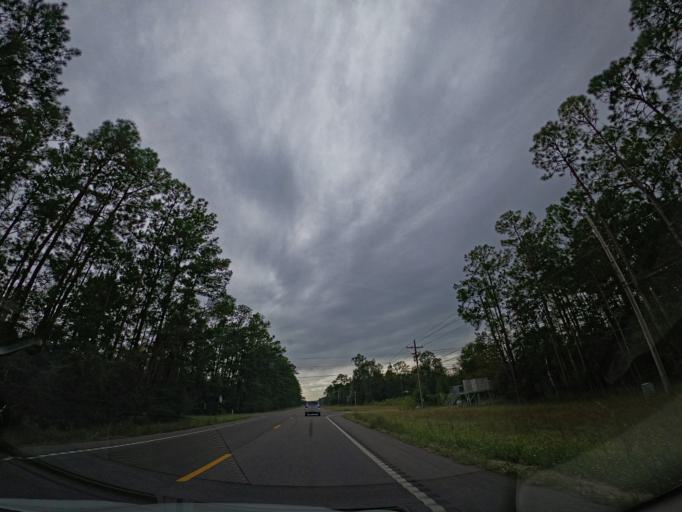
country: US
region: Mississippi
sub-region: Hancock County
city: Pearlington
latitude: 30.2478
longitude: -89.5957
